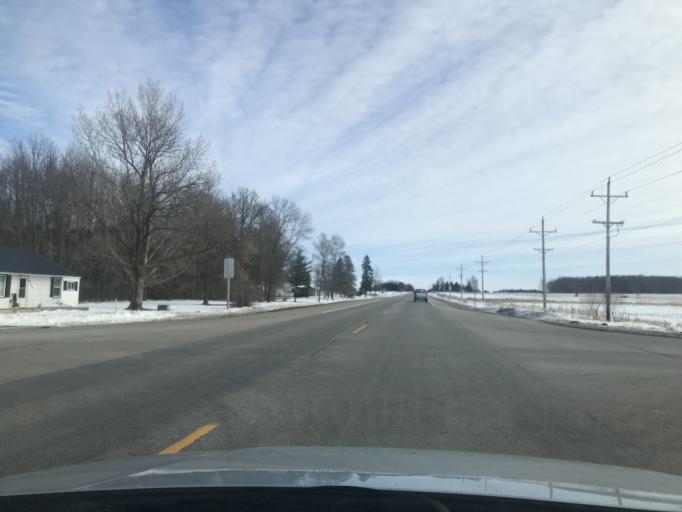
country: US
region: Wisconsin
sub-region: Oconto County
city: Oconto Falls
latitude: 44.8953
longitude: -88.2072
